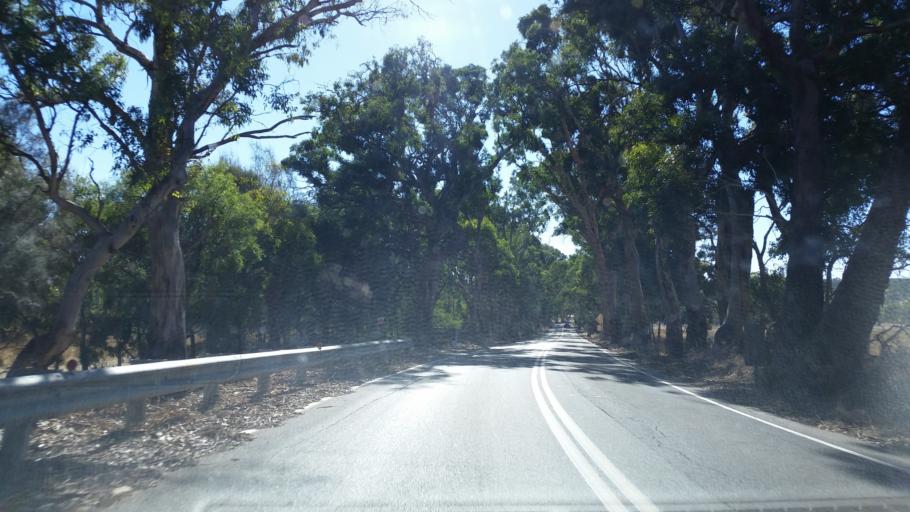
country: AU
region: South Australia
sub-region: Adelaide Hills
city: Birdwood
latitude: -34.8040
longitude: 139.0110
